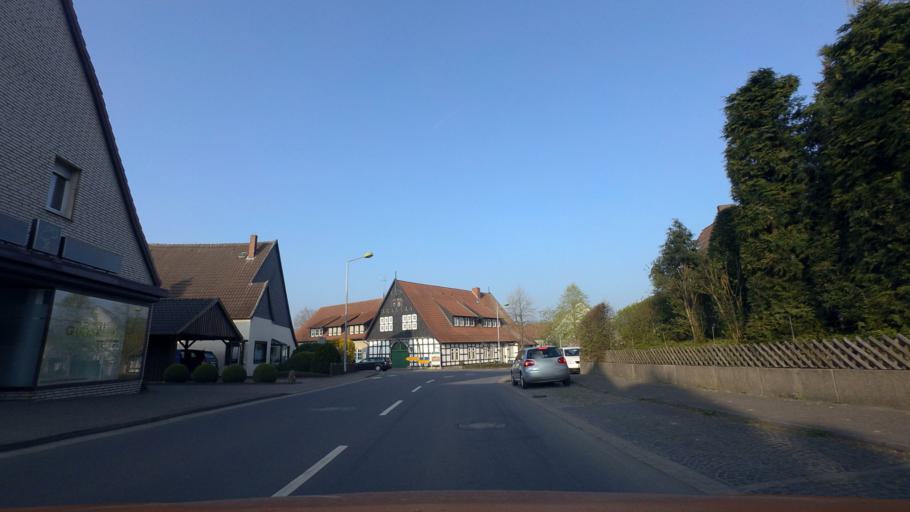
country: DE
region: Lower Saxony
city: Neuenkirchen
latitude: 52.1806
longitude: 8.4167
